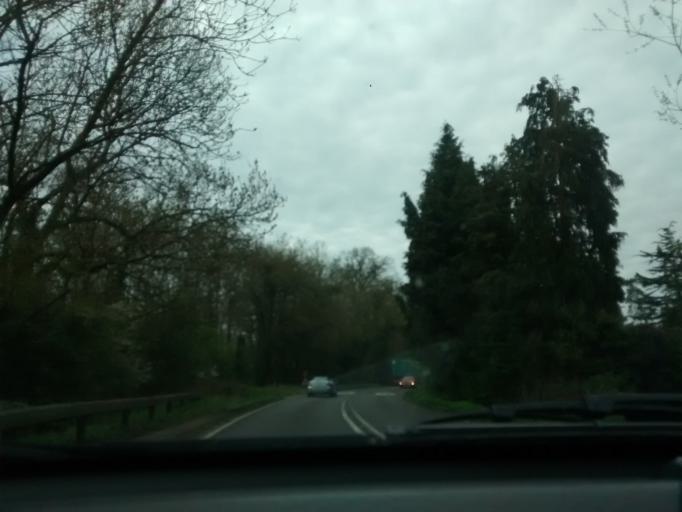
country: GB
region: England
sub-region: Oxfordshire
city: Bicester
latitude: 51.9537
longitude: -1.1083
